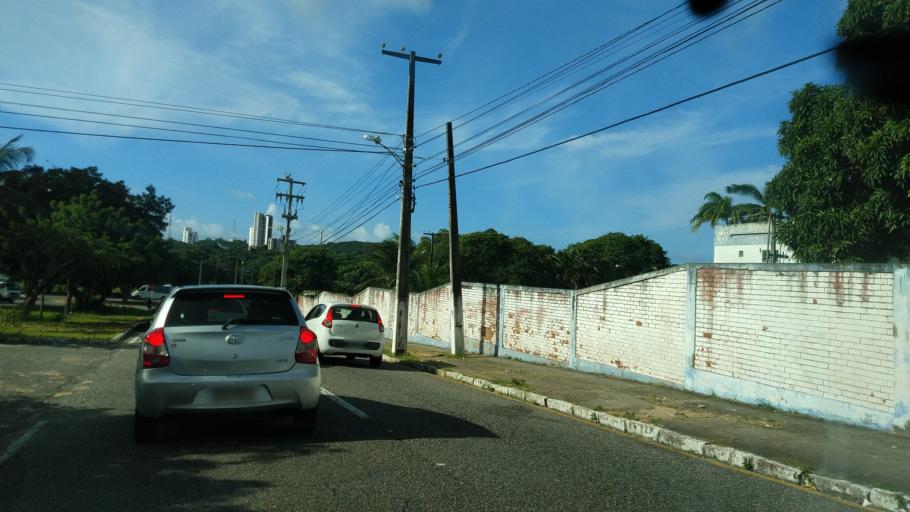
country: BR
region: Rio Grande do Norte
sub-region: Natal
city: Natal
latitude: -5.8094
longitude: -35.2006
